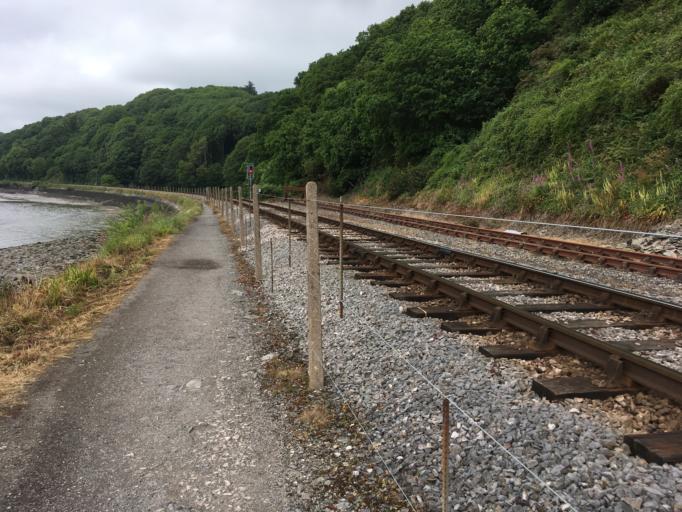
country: GB
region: England
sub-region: Devon
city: Dartmouth
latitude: 50.3547
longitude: -3.5700
